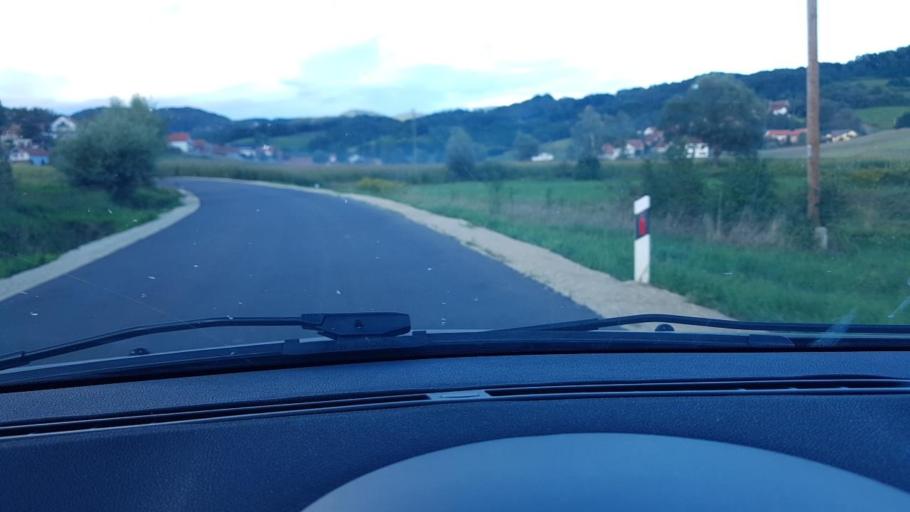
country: HR
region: Krapinsko-Zagorska
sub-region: Grad Krapina
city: Krapina
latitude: 46.1430
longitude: 15.8173
